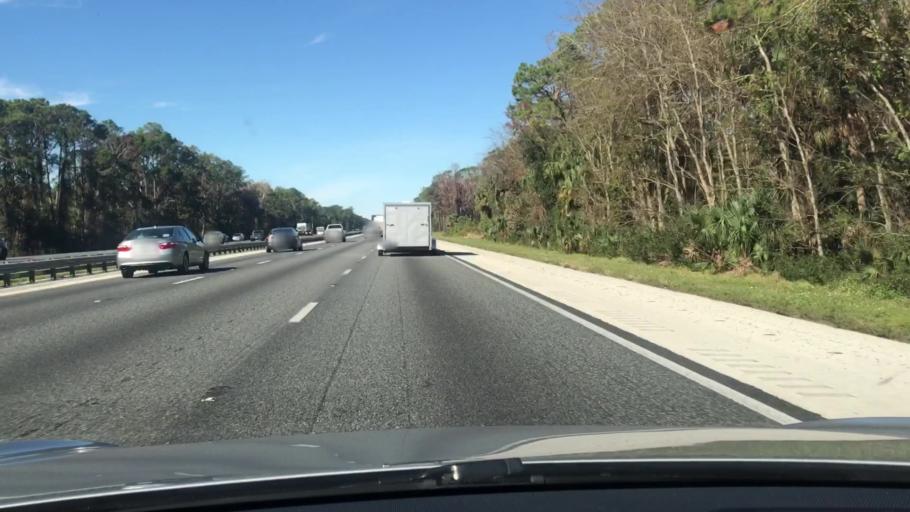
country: US
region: Florida
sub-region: Volusia County
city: Ormond-by-the-Sea
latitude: 29.3706
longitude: -81.1406
